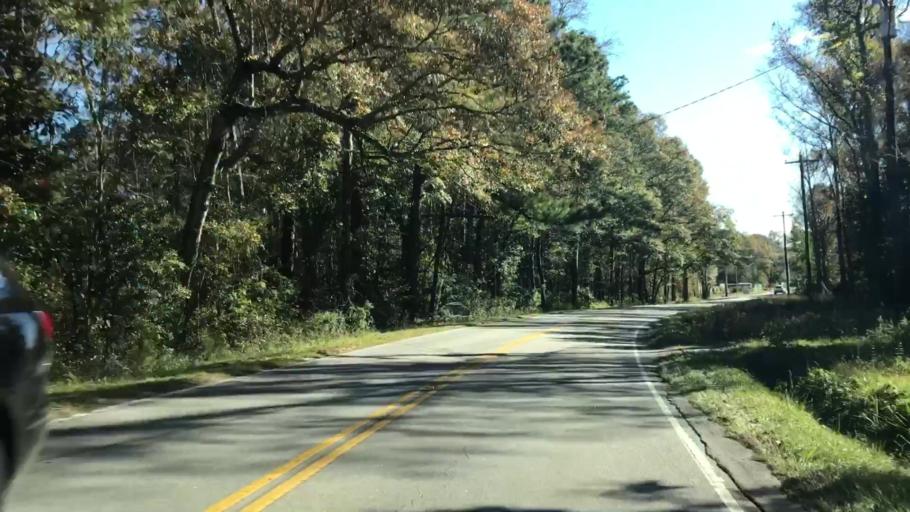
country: US
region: South Carolina
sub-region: Dorchester County
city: Summerville
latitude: 33.0206
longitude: -80.2218
